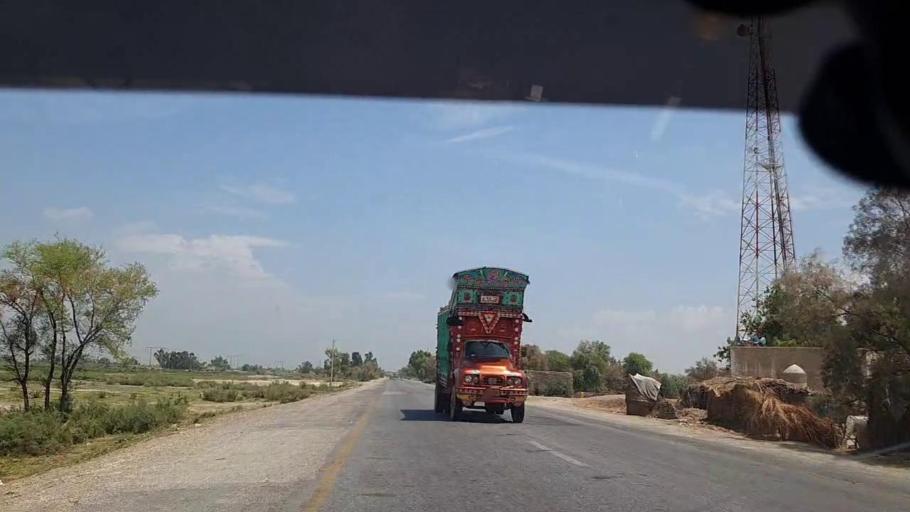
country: PK
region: Sindh
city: Ghauspur
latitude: 28.0883
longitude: 68.9643
